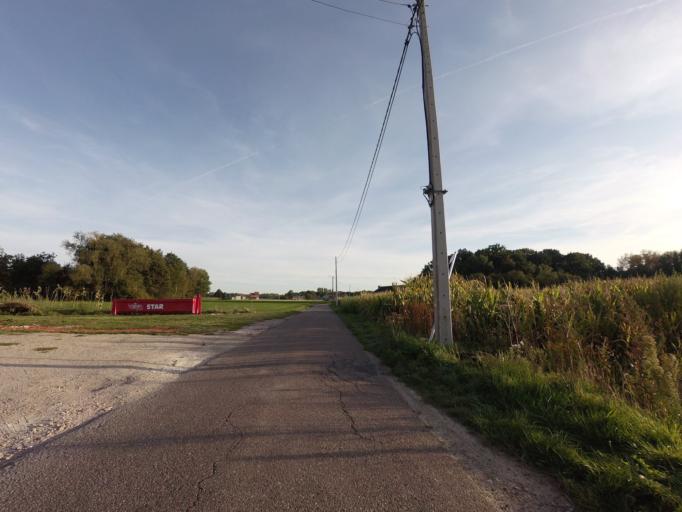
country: BE
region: Flanders
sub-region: Provincie Vlaams-Brabant
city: Kampenhout
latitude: 50.9395
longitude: 4.5893
